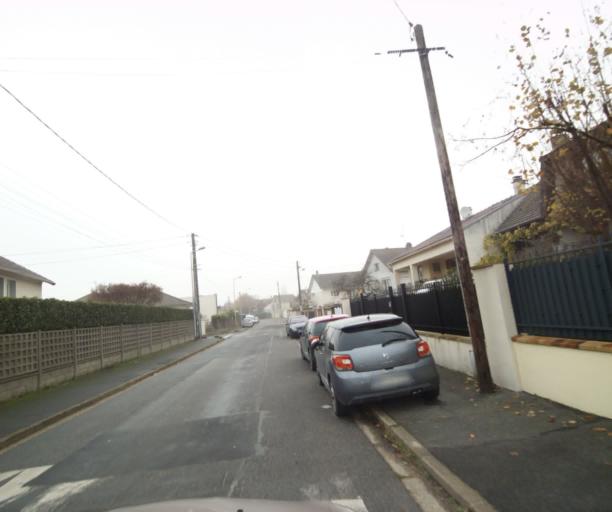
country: FR
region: Ile-de-France
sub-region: Departement de Seine-Saint-Denis
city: Coubron
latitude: 48.9096
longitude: 2.5886
